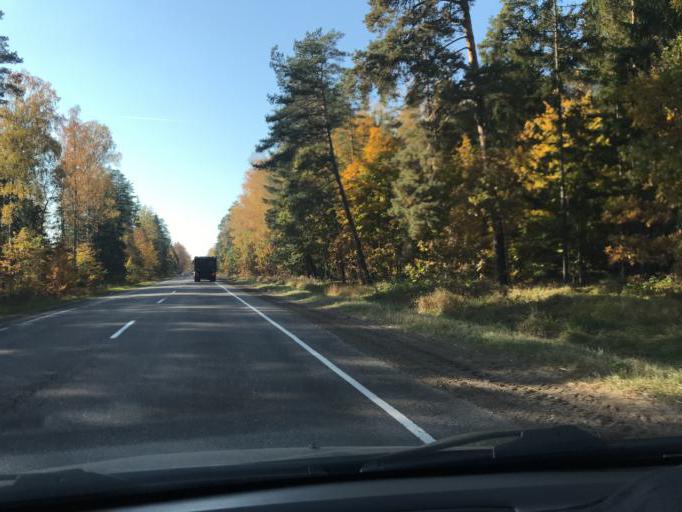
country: BY
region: Mogilev
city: Hlusha
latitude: 53.0889
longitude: 28.8800
